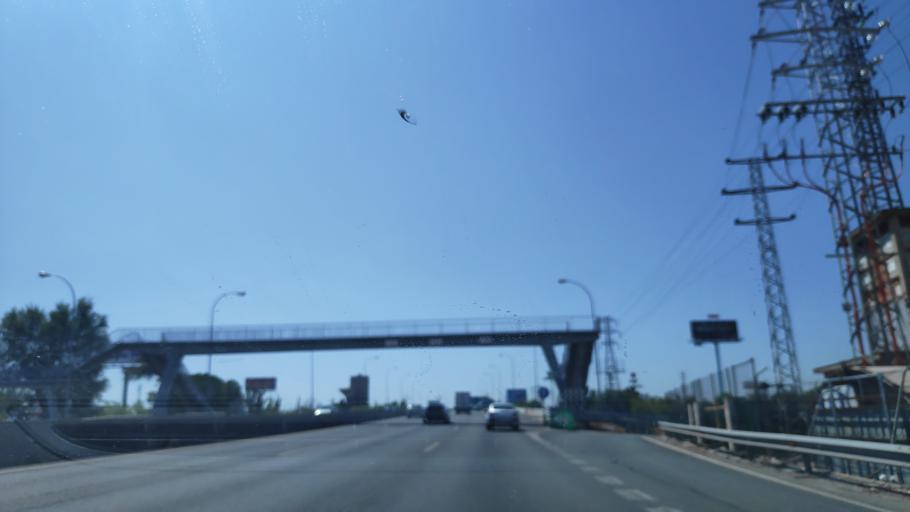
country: ES
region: Madrid
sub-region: Provincia de Madrid
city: Villaverde
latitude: 40.3450
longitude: -3.7236
